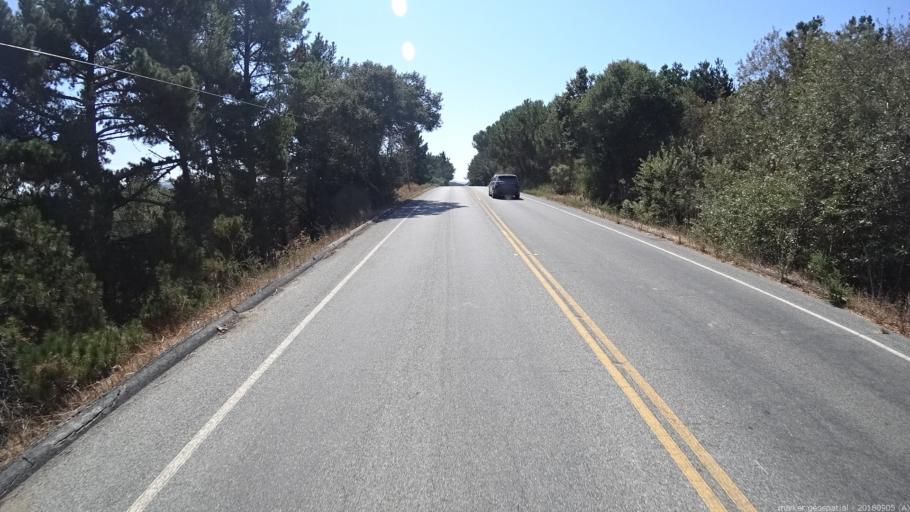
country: US
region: California
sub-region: Monterey County
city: Carmel Valley Village
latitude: 36.5430
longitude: -121.7536
